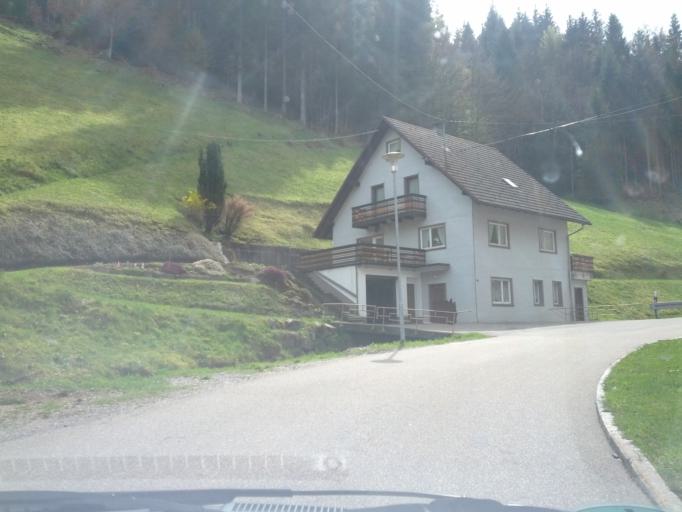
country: DE
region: Baden-Wuerttemberg
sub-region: Freiburg Region
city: Sankt Margen
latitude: 48.0007
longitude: 8.1355
